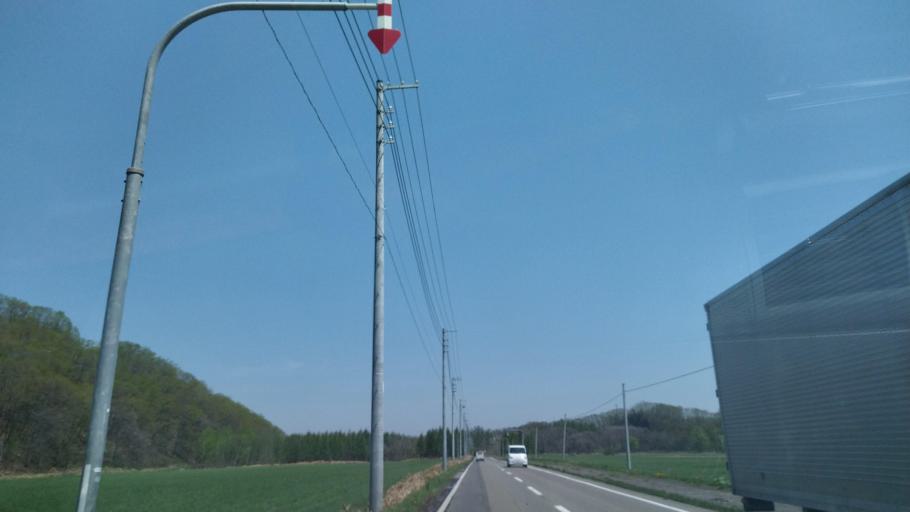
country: JP
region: Hokkaido
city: Obihiro
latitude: 42.8211
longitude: 142.9842
